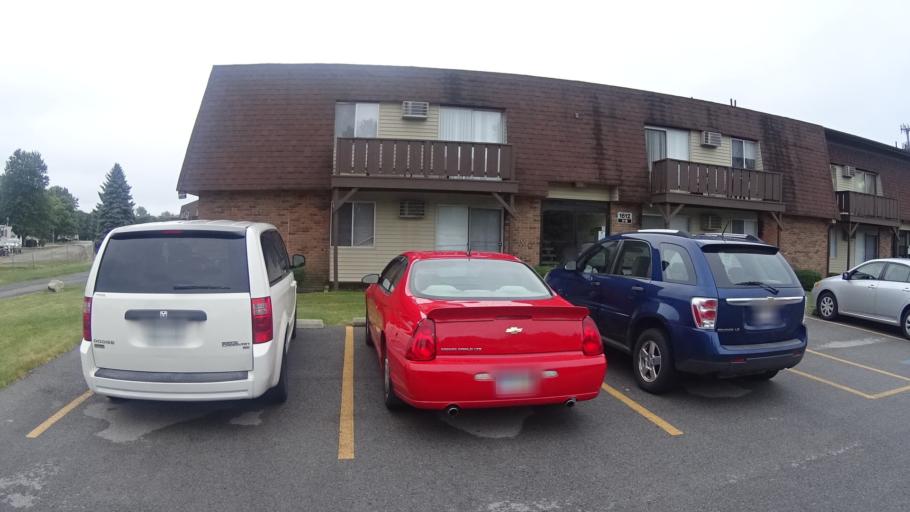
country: US
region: Ohio
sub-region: Erie County
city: Sandusky
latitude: 41.4395
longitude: -82.6690
